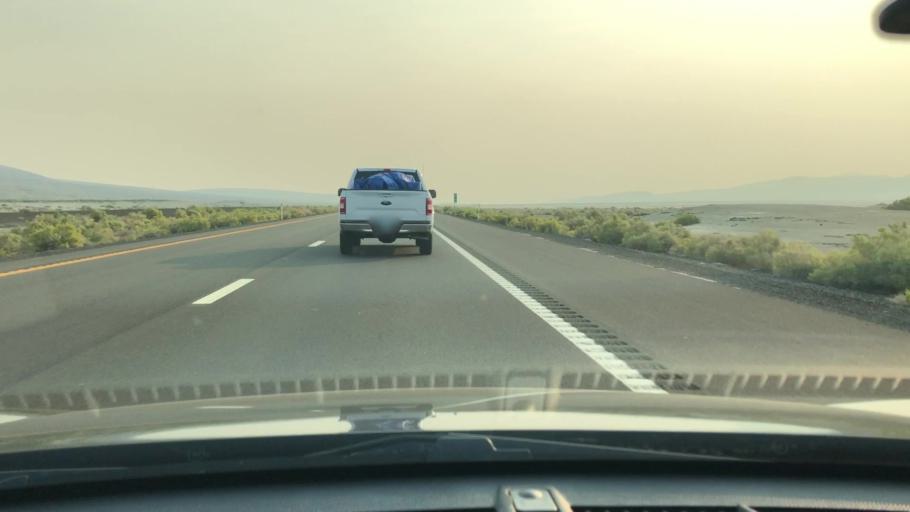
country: US
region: Nevada
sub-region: Lyon County
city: Fernley
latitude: 39.6547
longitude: -119.1606
